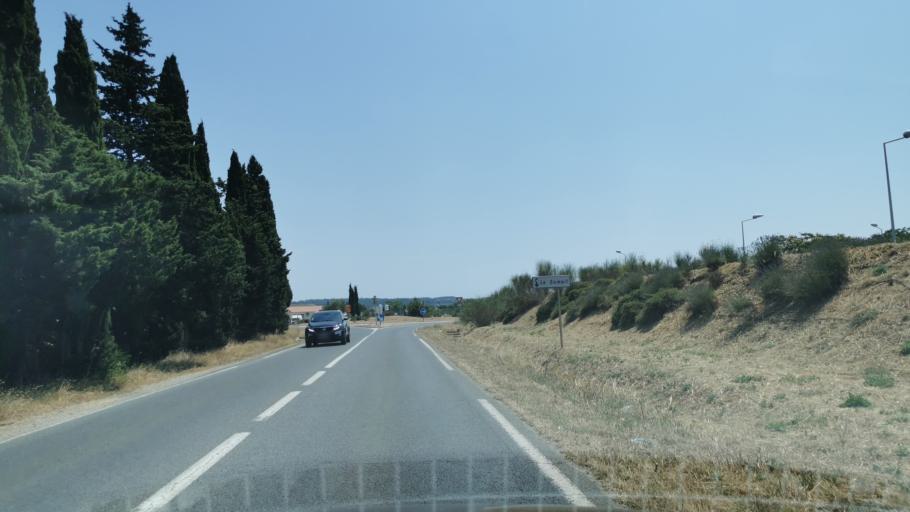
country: FR
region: Languedoc-Roussillon
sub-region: Departement de l'Aude
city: Saint-Marcel-sur-Aude
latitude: 43.2569
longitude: 2.9097
